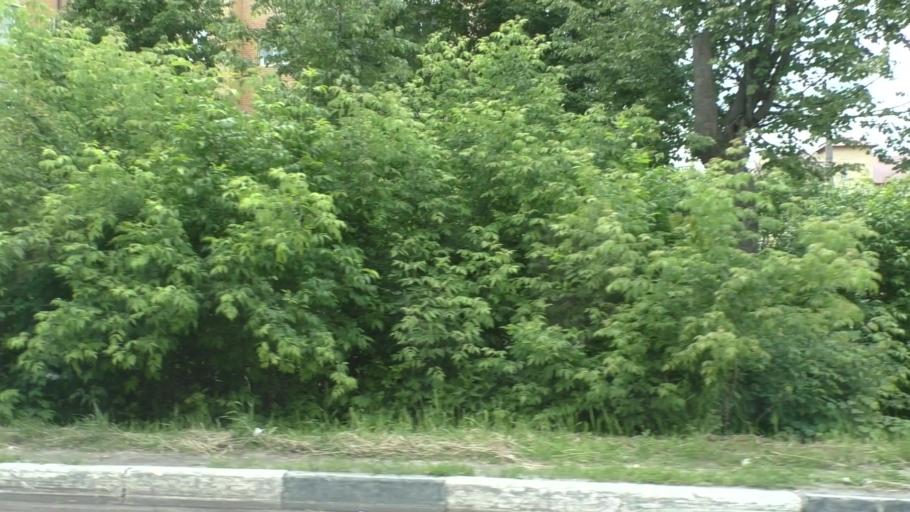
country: RU
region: Moskovskaya
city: Yegor'yevsk
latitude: 55.3934
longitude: 39.0204
